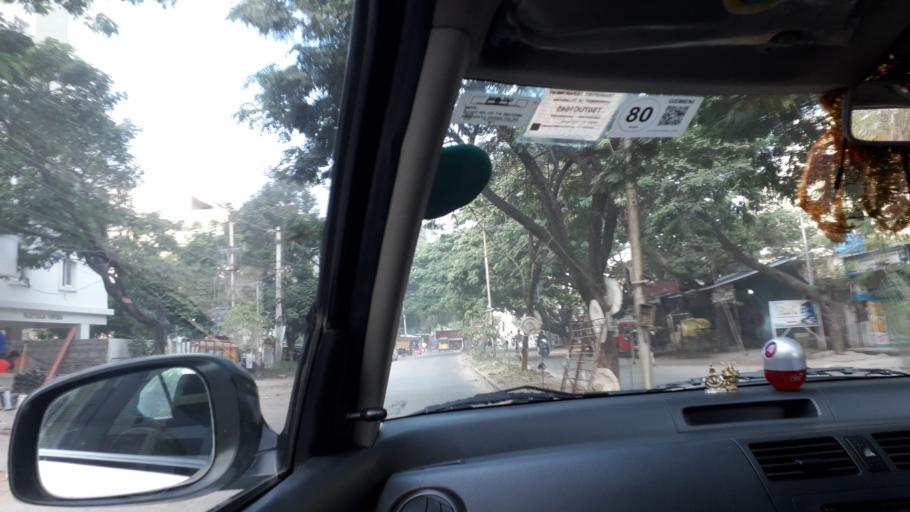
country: IN
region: Telangana
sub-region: Hyderabad
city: Hyderabad
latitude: 17.3935
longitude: 78.3776
